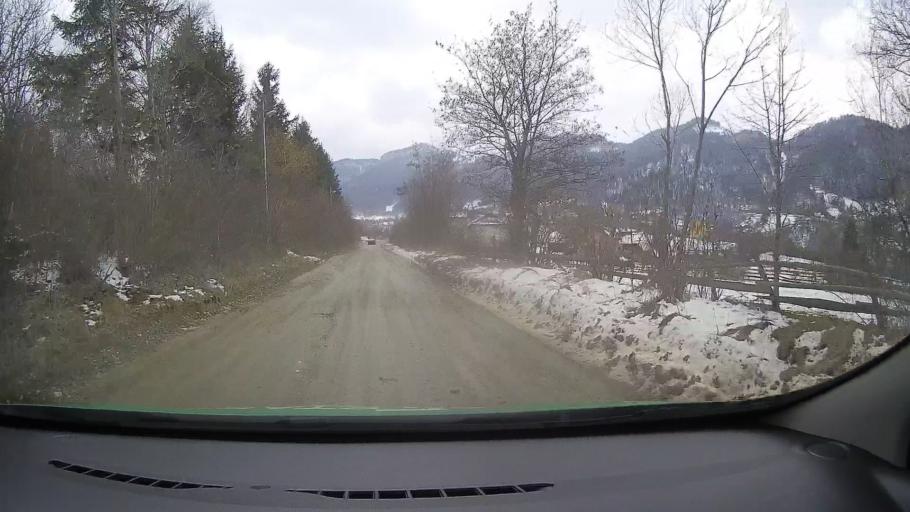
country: RO
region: Brasov
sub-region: Comuna Zarnesti
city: Zarnesti
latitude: 45.5476
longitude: 25.3221
